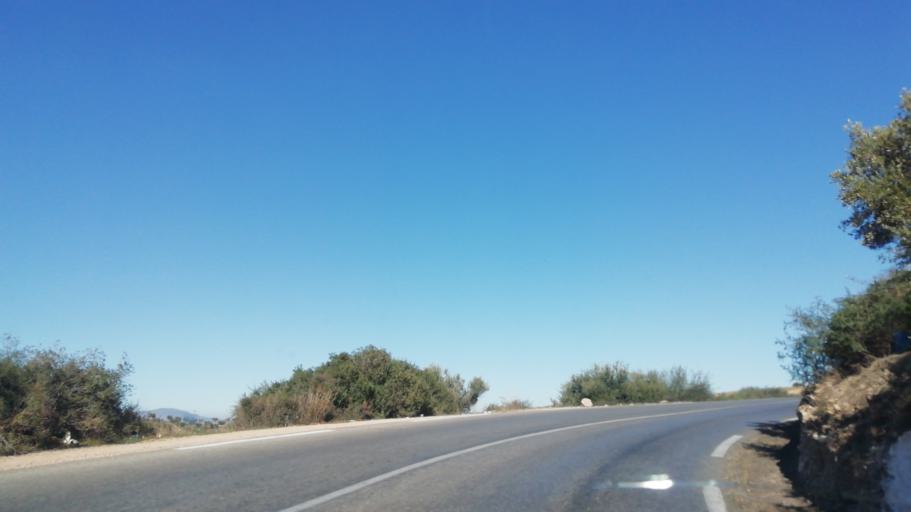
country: DZ
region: Tlemcen
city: Beni Mester
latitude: 34.8262
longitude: -1.5850
